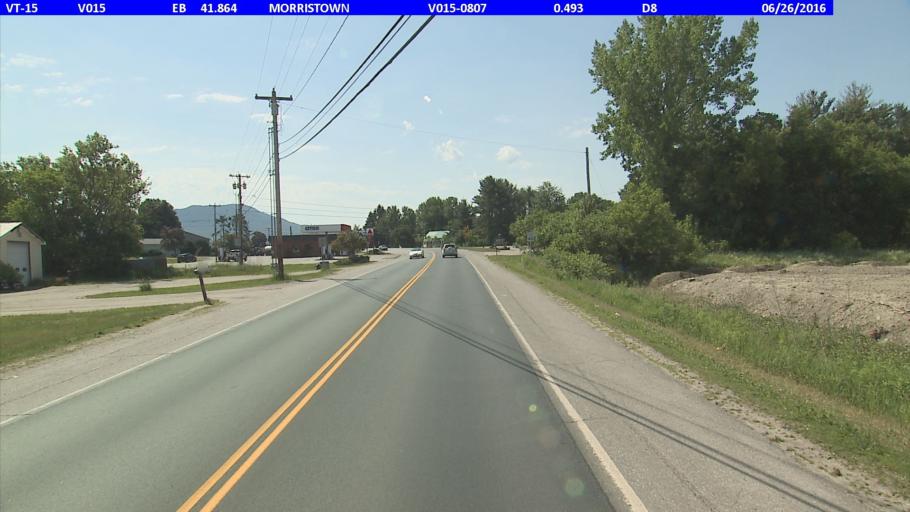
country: US
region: Vermont
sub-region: Lamoille County
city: Morrisville
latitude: 44.5797
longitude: -72.5973
